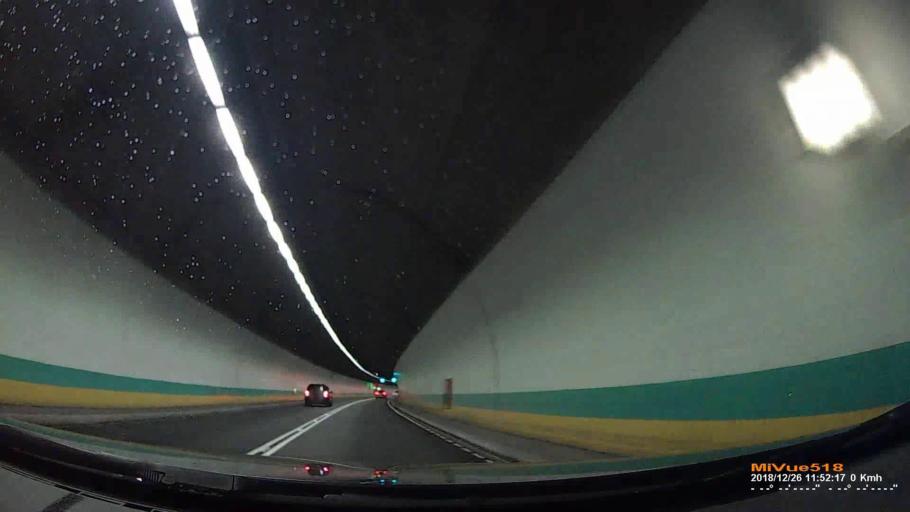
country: TW
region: Taiwan
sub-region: Keelung
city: Keelung
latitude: 24.9681
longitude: 121.6835
